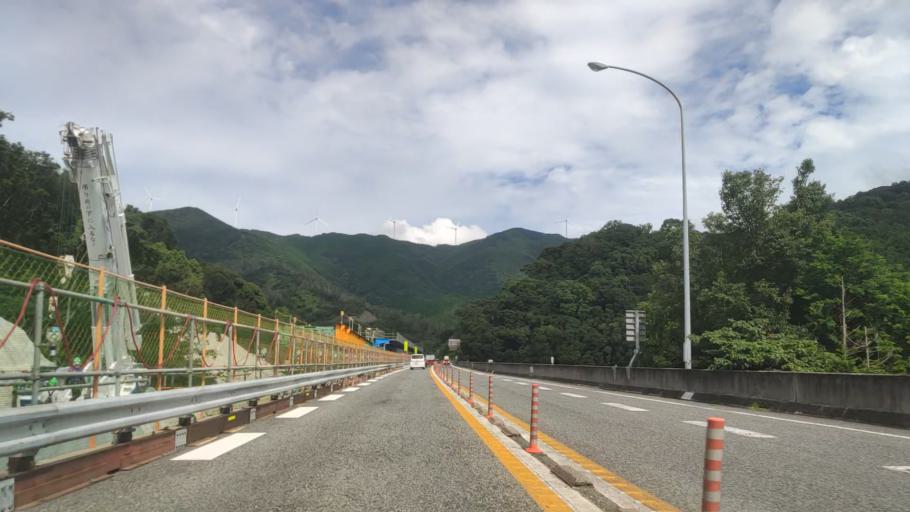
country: JP
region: Wakayama
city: Gobo
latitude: 33.9372
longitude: 135.1961
